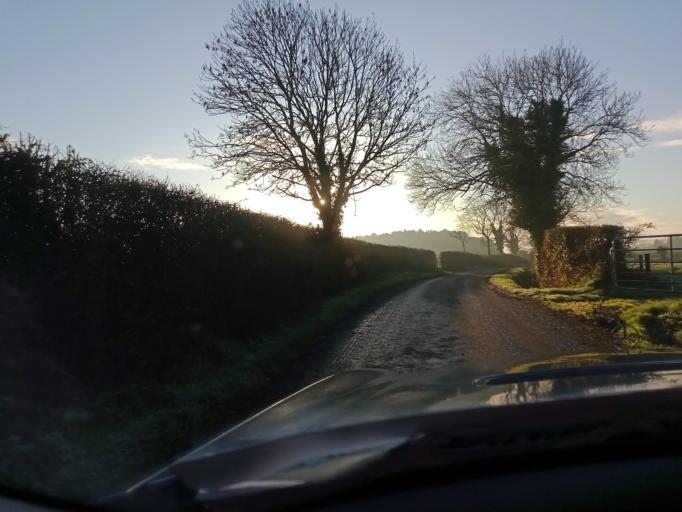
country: IE
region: Leinster
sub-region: Kilkenny
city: Callan
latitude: 52.5365
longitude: -7.4305
